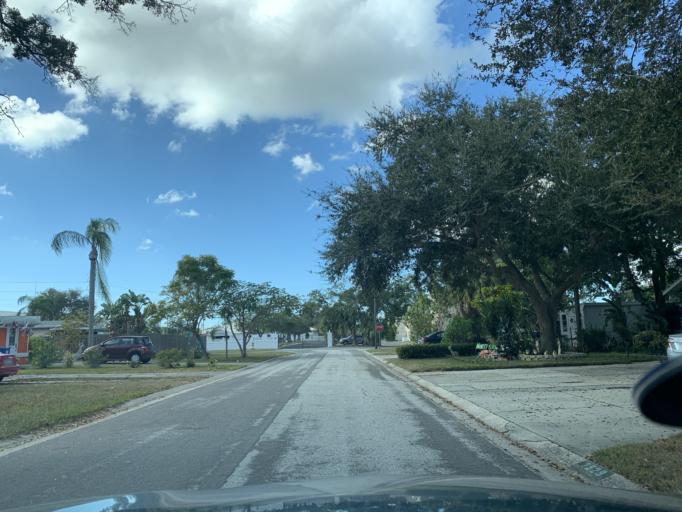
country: US
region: Florida
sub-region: Pinellas County
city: Kenneth City
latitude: 27.8055
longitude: -82.7426
